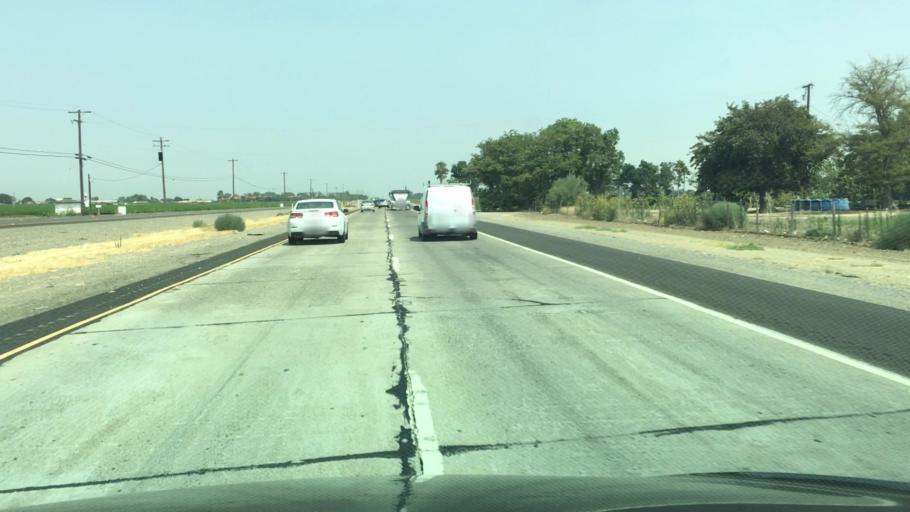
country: US
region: California
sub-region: Merced County
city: Los Banos
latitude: 37.0566
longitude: -120.9096
